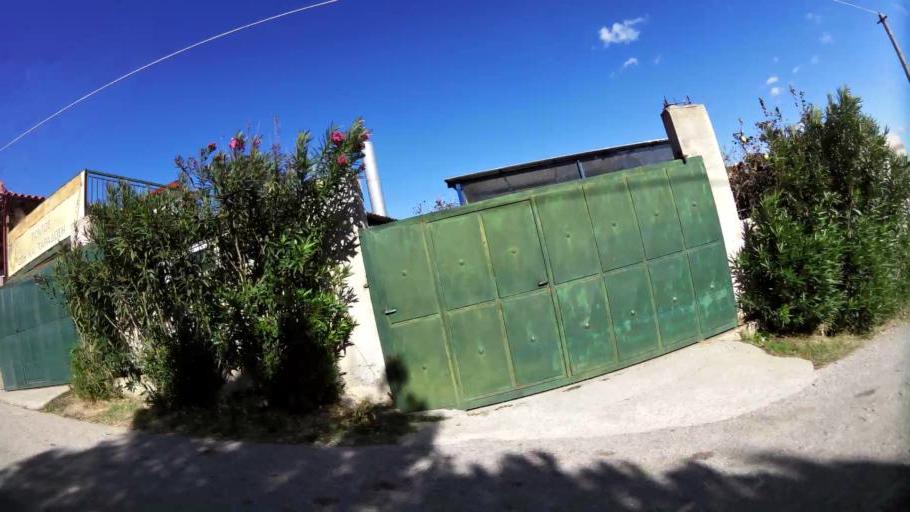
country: GR
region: Attica
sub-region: Nomarchia Anatolikis Attikis
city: Acharnes
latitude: 38.1089
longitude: 23.7182
